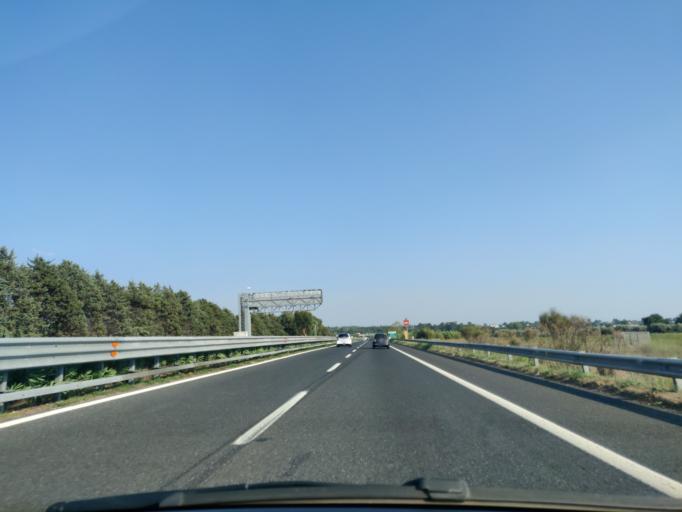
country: IT
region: Latium
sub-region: Citta metropolitana di Roma Capitale
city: Cerveteri
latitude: 41.9716
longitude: 12.1045
